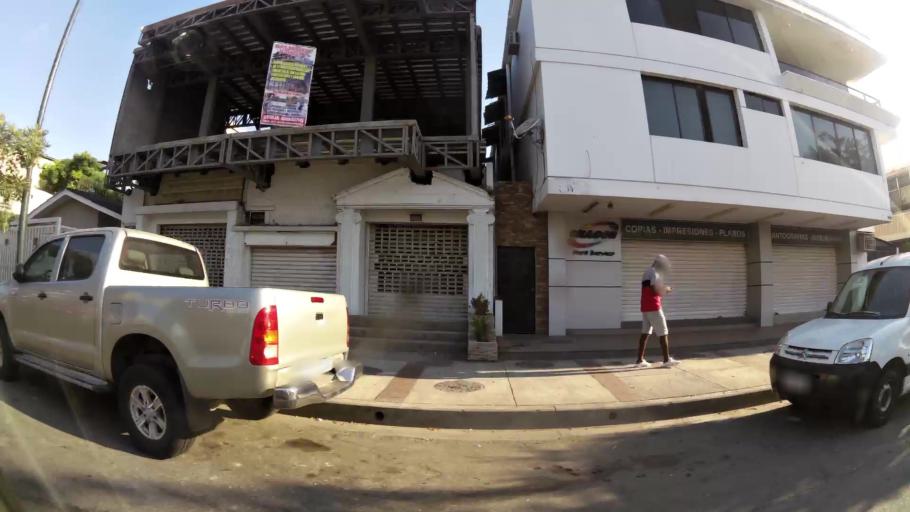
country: EC
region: Guayas
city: Guayaquil
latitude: -2.1622
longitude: -79.9149
